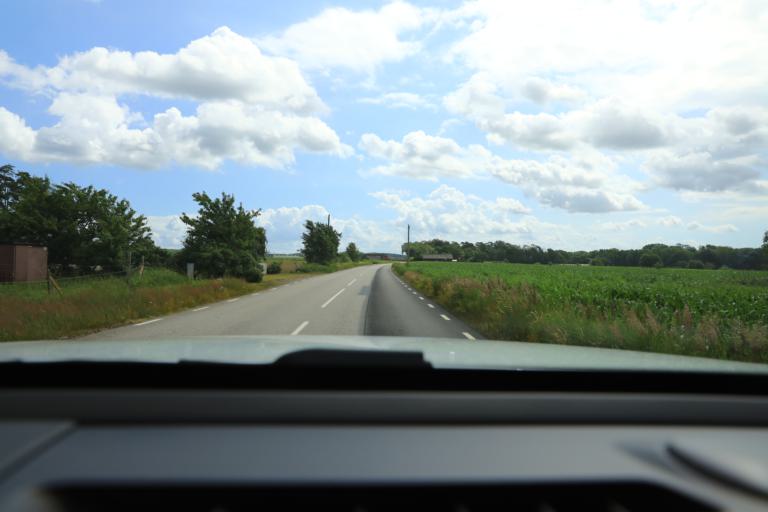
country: SE
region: Halland
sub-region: Varbergs Kommun
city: Tvaaker
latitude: 57.0415
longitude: 12.4308
